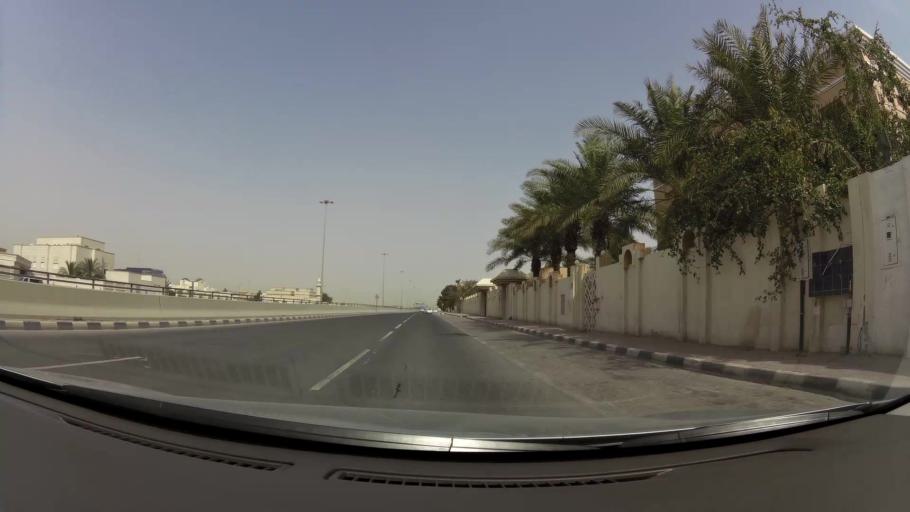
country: QA
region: Baladiyat ad Dawhah
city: Doha
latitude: 25.2768
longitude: 51.4886
